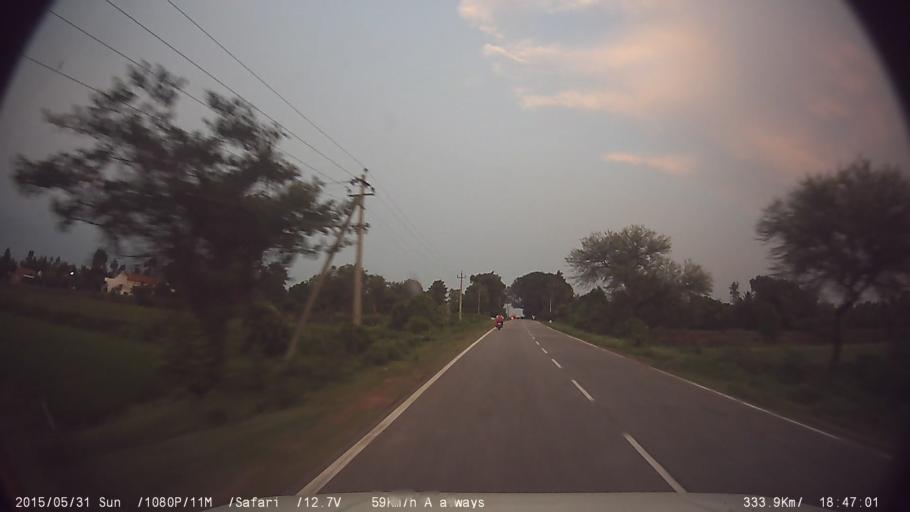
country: IN
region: Karnataka
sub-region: Mysore
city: Tirumakudal Narsipur
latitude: 12.1631
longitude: 76.8380
